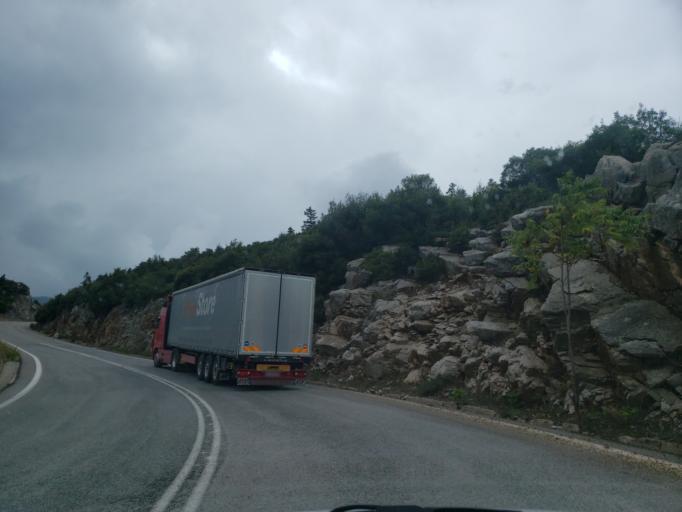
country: GR
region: Central Greece
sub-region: Nomos Fokidos
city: Amfissa
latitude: 38.6443
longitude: 22.3963
